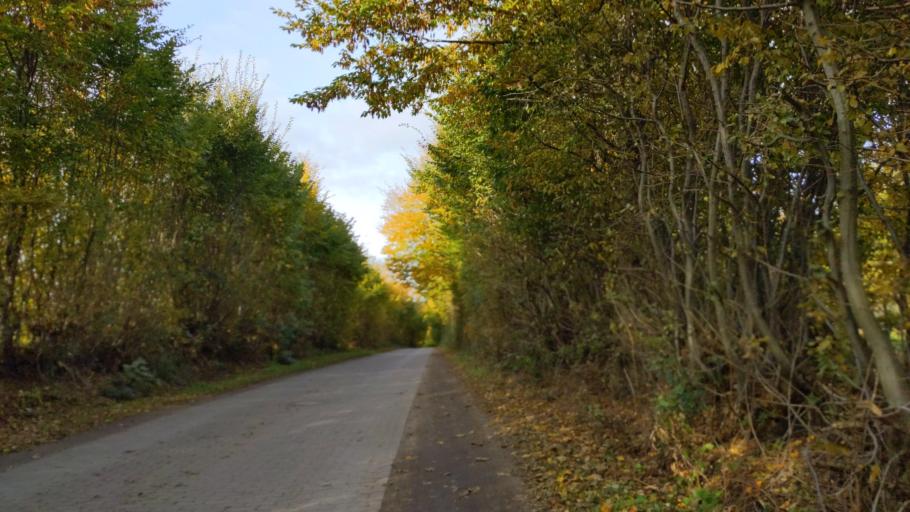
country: DE
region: Schleswig-Holstein
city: Eutin
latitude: 54.1494
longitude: 10.6293
